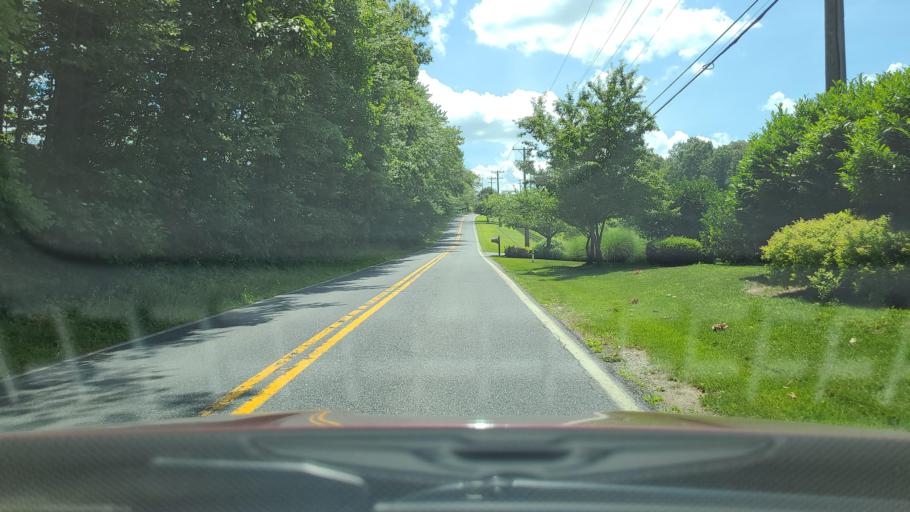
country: US
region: Maryland
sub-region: Montgomery County
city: Clarksburg
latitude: 39.2505
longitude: -77.2705
